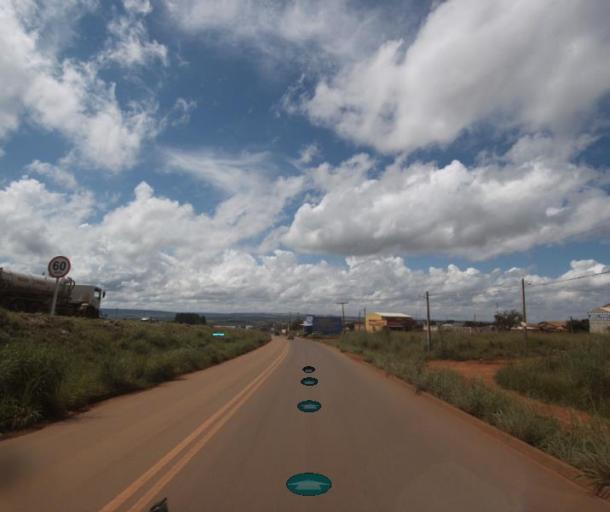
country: BR
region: Federal District
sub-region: Brasilia
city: Brasilia
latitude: -15.7593
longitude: -48.2505
